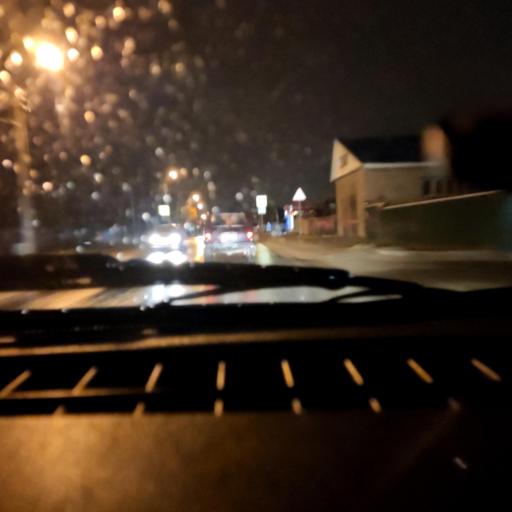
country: RU
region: Bashkortostan
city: Ufa
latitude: 54.8197
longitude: 56.1717
